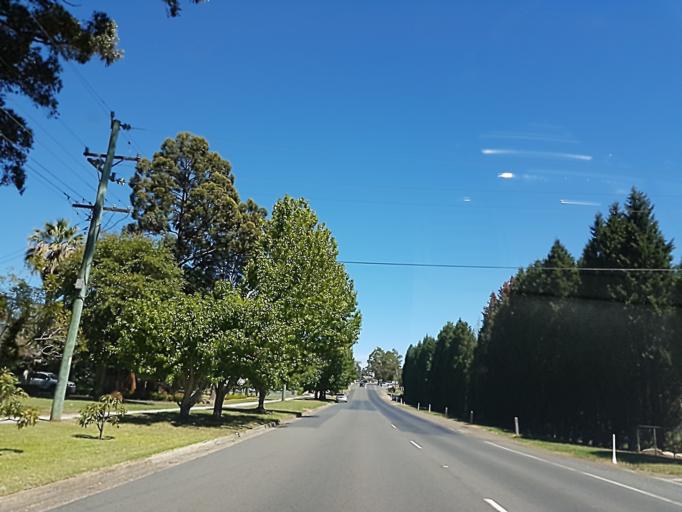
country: AU
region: New South Wales
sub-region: Hornsby Shire
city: Glenorie
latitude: -33.6035
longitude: 151.0112
